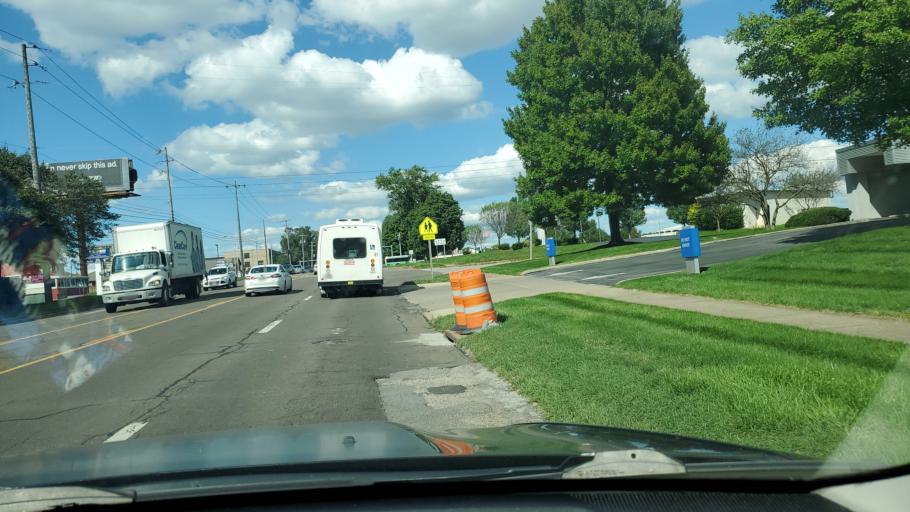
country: US
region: Ohio
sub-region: Mahoning County
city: Boardman
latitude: 41.0171
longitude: -80.6627
